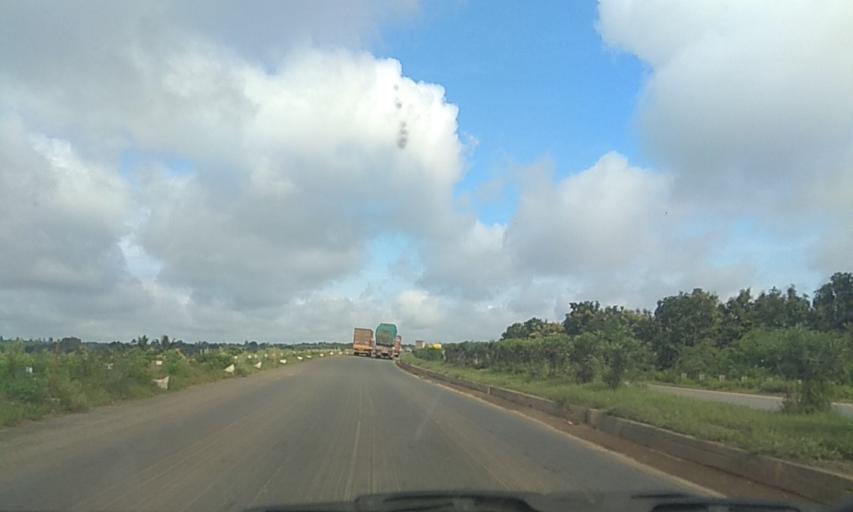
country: IN
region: Karnataka
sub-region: Haveri
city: Shiggaon
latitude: 15.0165
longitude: 75.1876
